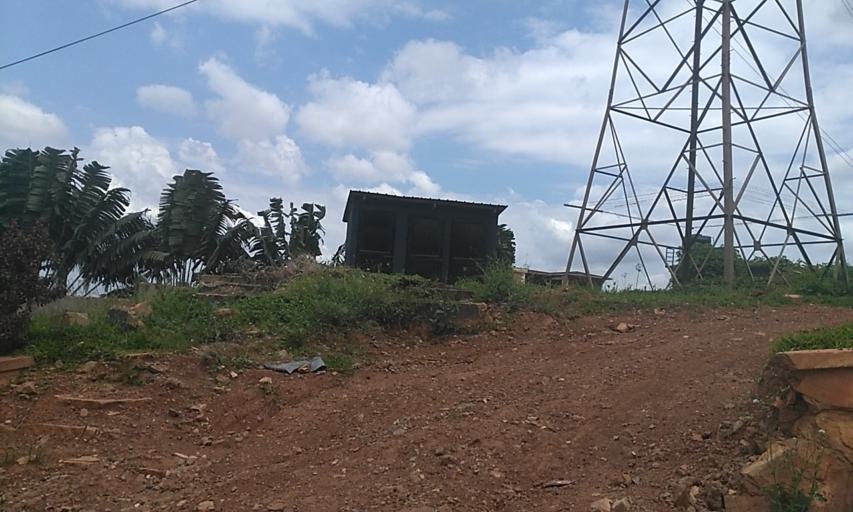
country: UG
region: Central Region
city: Kampala Central Division
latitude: 0.3488
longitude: 32.6032
